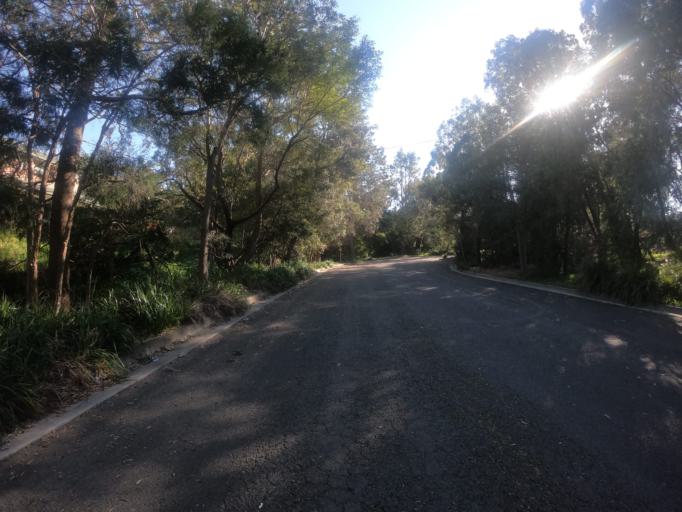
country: AU
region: New South Wales
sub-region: Hunters Hill
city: Gladesville
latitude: -33.8251
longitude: 151.1157
